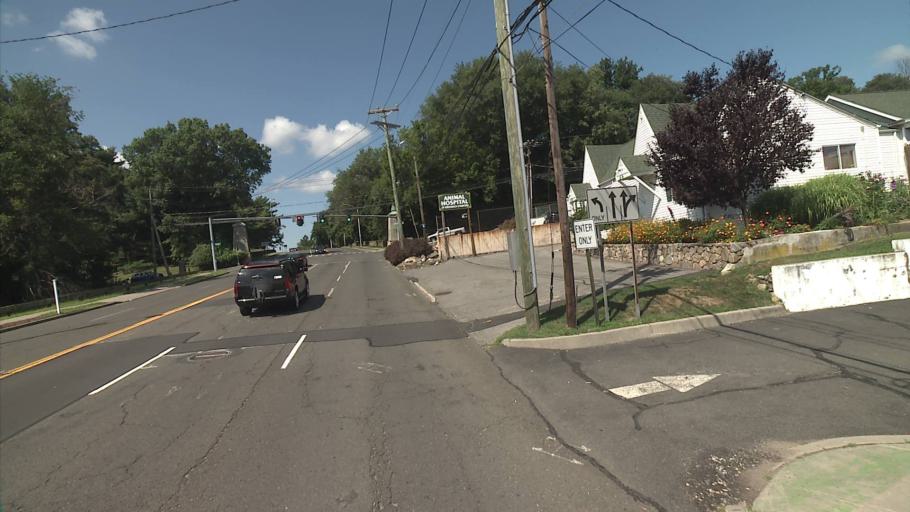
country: US
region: Connecticut
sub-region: Fairfield County
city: Riverside
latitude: 41.0486
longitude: -73.5655
